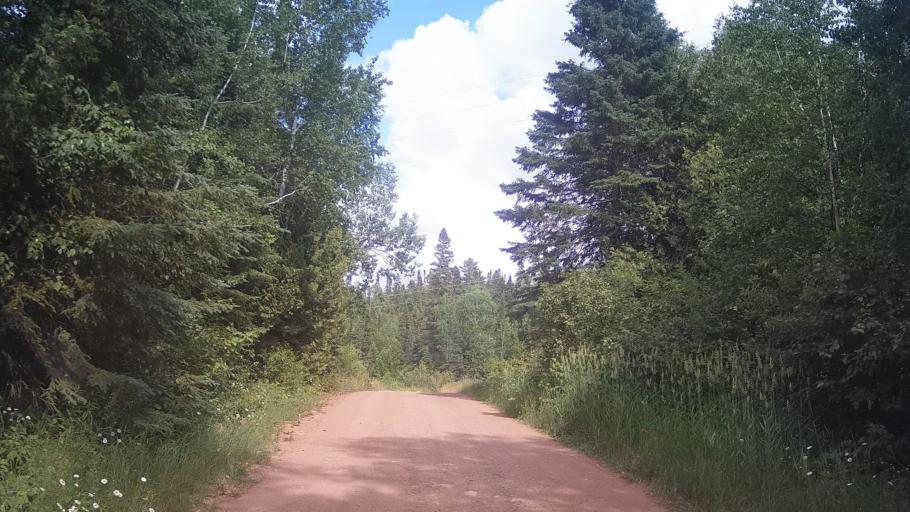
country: CA
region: Ontario
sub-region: Thunder Bay District
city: Thunder Bay
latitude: 48.6708
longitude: -88.6673
